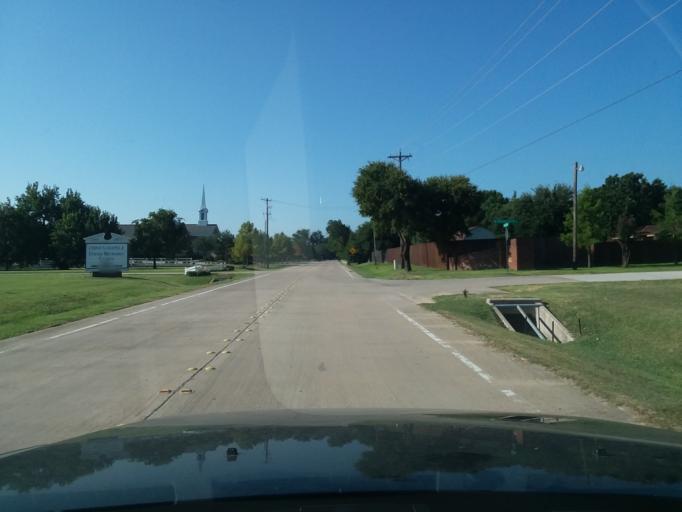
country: US
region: Texas
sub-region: Denton County
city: Copper Canyon
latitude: 33.0818
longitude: -97.0858
